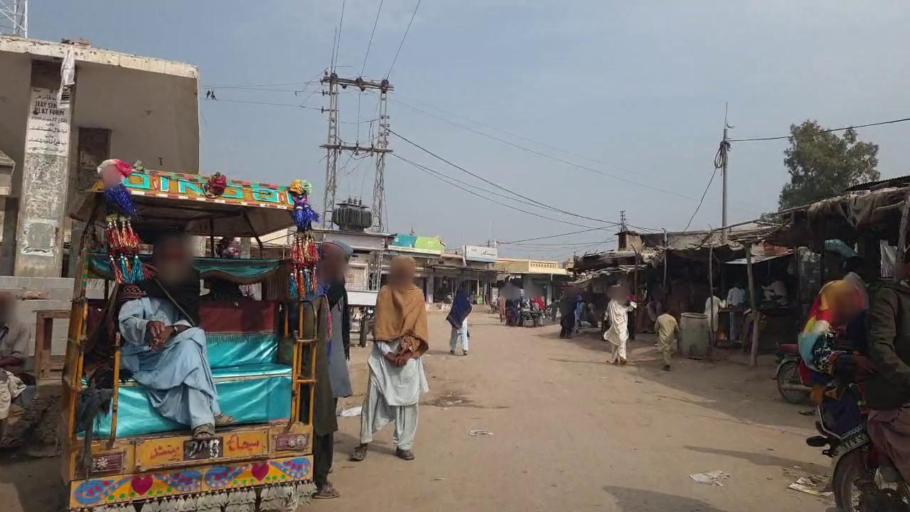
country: PK
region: Sindh
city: Sann
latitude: 26.0402
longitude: 68.1376
